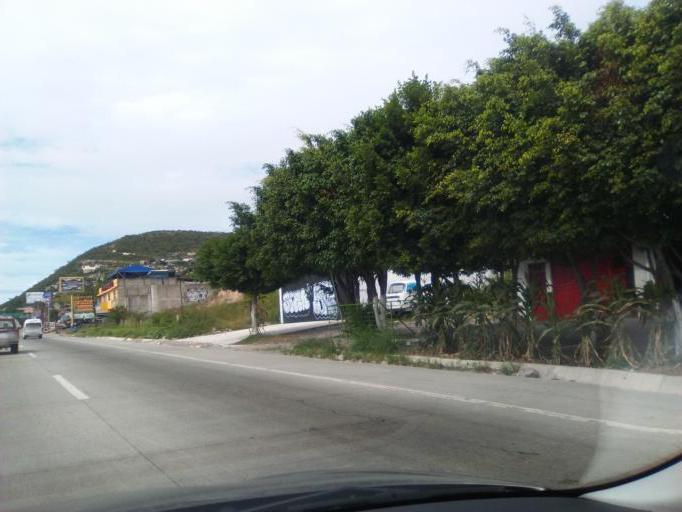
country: MX
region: Guerrero
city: Chilpancingo de los Bravos
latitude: 17.5845
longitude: -99.5158
